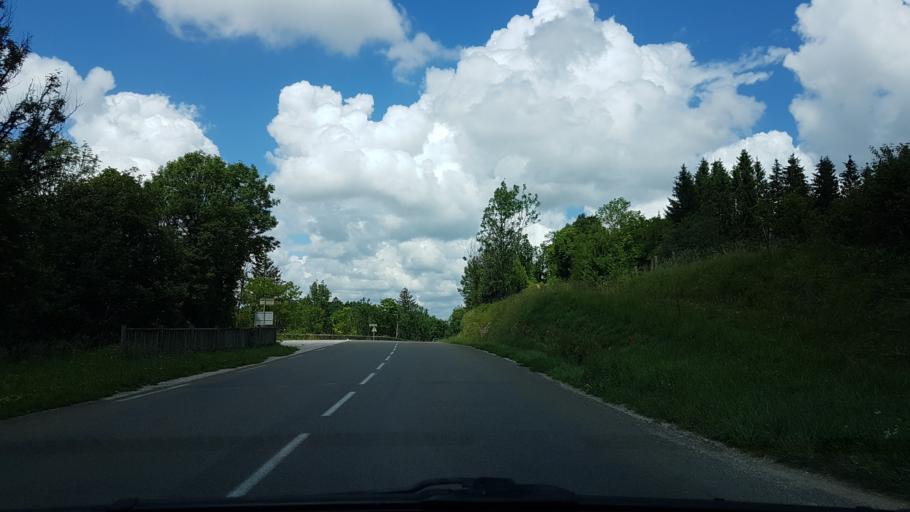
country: FR
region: Franche-Comte
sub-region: Departement du Jura
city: Clairvaux-les-Lacs
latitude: 46.5465
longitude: 5.7480
